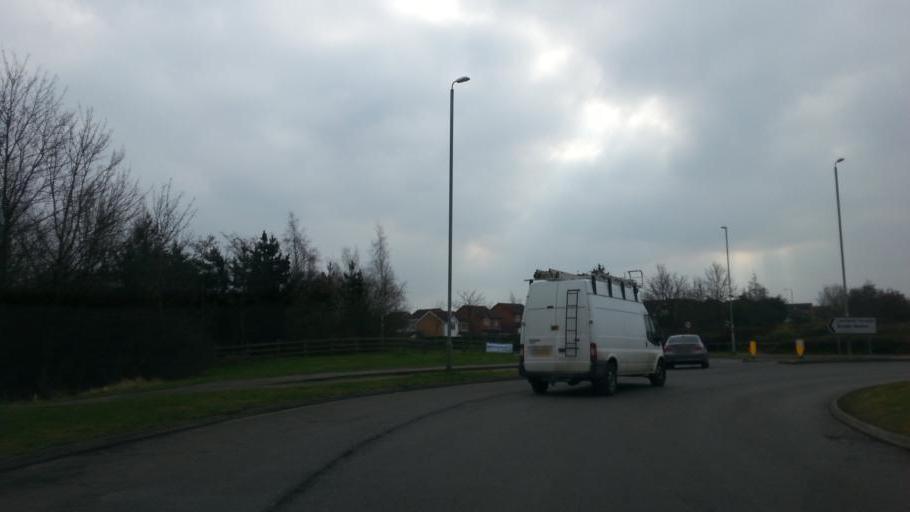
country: GB
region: England
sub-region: Northamptonshire
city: Corby
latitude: 52.4729
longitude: -0.7176
